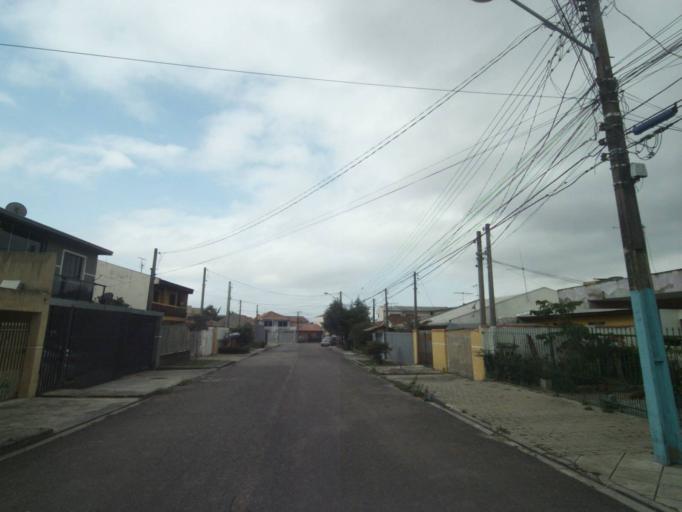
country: BR
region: Parana
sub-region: Sao Jose Dos Pinhais
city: Sao Jose dos Pinhais
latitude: -25.5418
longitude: -49.2569
